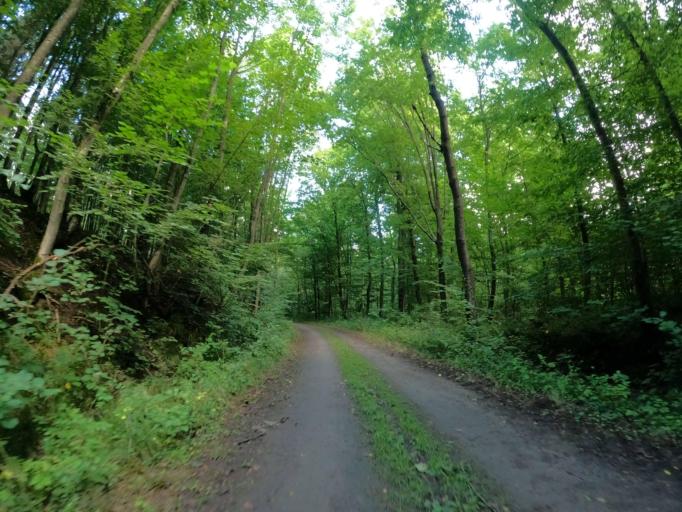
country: DE
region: Mecklenburg-Vorpommern
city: Sehlen
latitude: 54.3568
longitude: 13.4131
